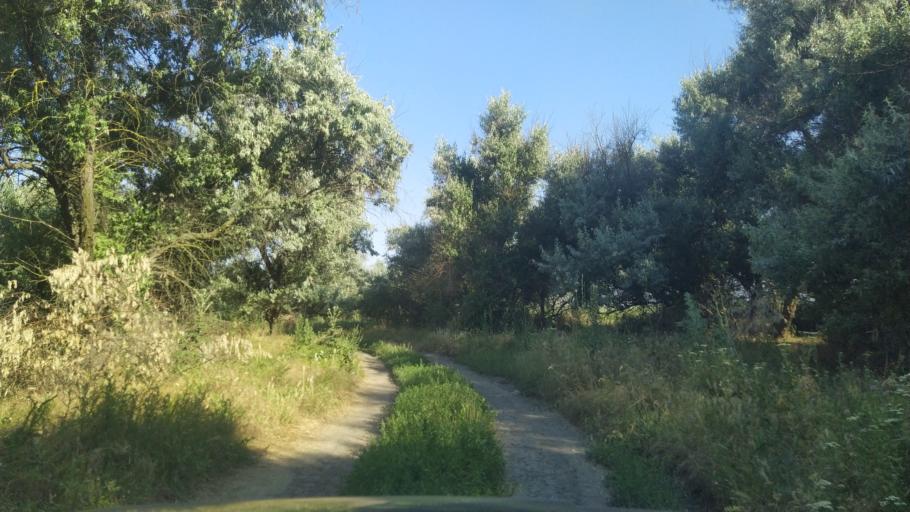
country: RU
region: Rostov
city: Kuleshovka
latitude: 47.1363
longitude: 39.6393
